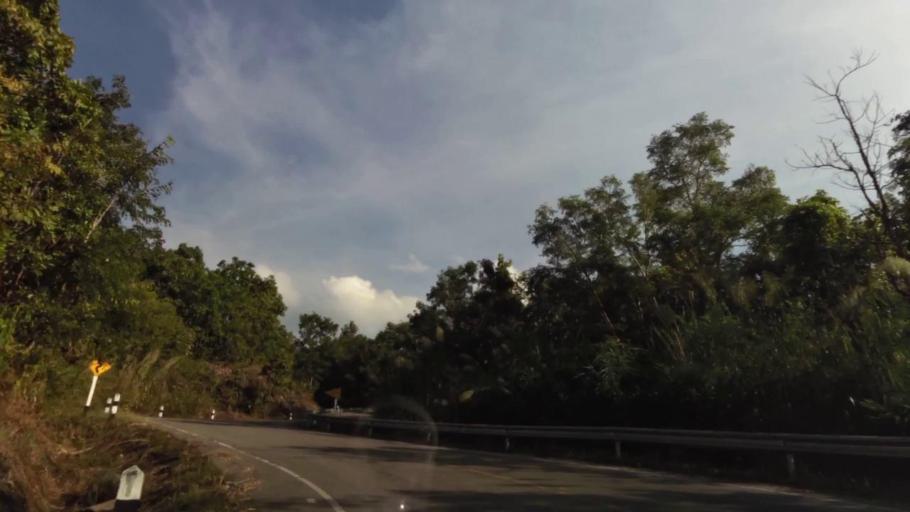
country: TH
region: Chiang Rai
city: Khun Tan
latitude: 19.8797
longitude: 100.3082
